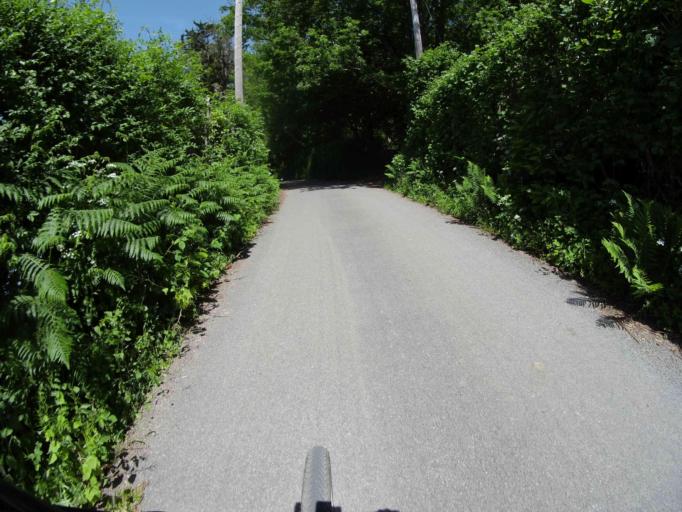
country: GB
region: England
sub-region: Devon
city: Bovey Tracey
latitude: 50.6131
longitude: -3.7114
